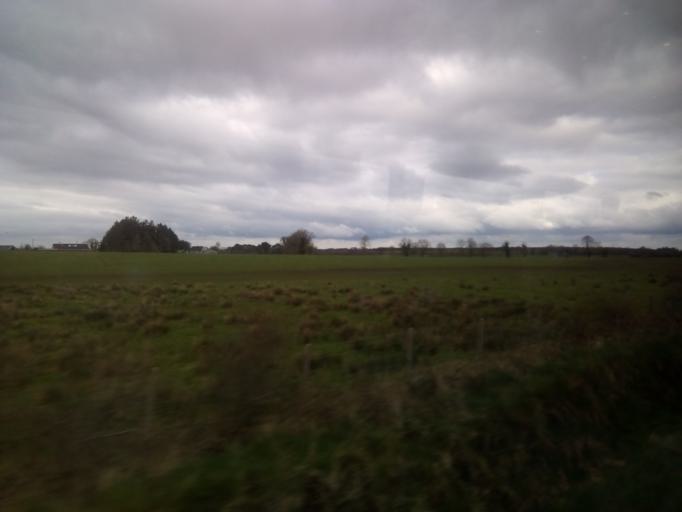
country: IE
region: Leinster
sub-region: An Longfort
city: Edgeworthstown
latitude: 53.6752
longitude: -7.5281
